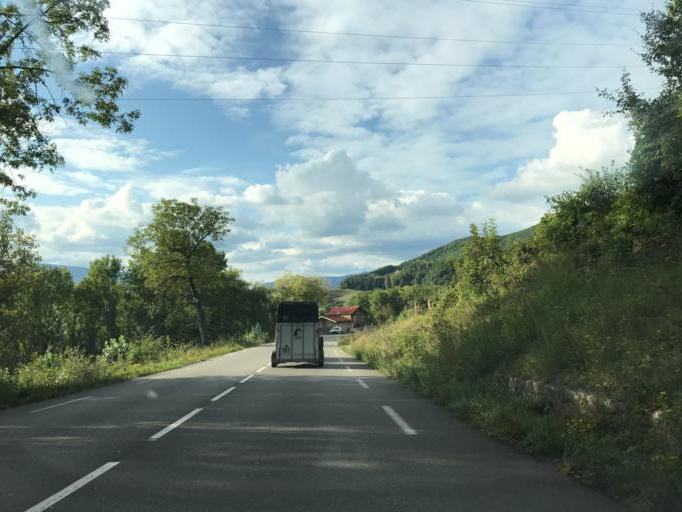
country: FR
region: Rhone-Alpes
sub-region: Departement de l'Ain
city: Bellegarde-sur-Valserine
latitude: 46.0980
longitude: 5.8456
